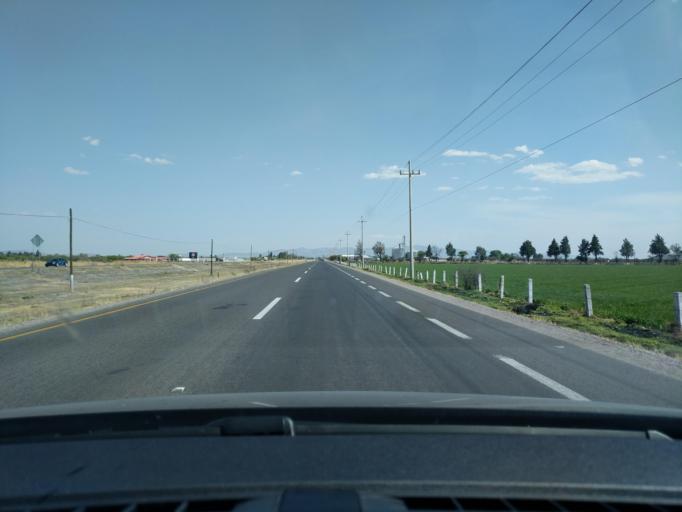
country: MX
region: Durango
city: Victoria de Durango
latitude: 24.0891
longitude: -104.5673
